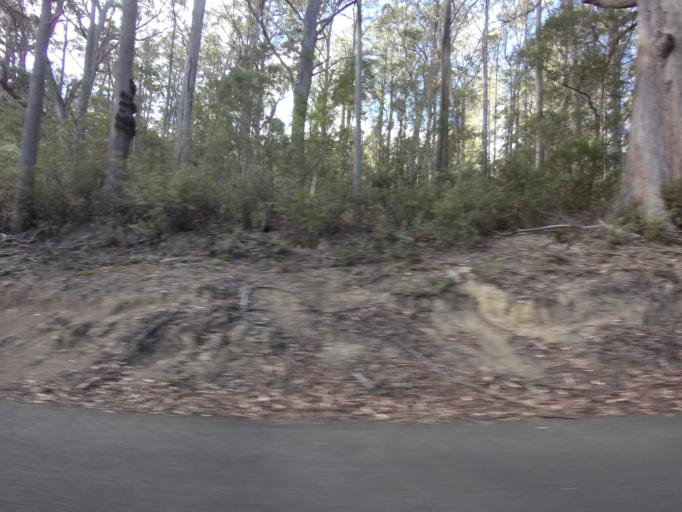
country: AU
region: Tasmania
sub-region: Break O'Day
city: St Helens
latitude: -41.6337
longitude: 148.2381
